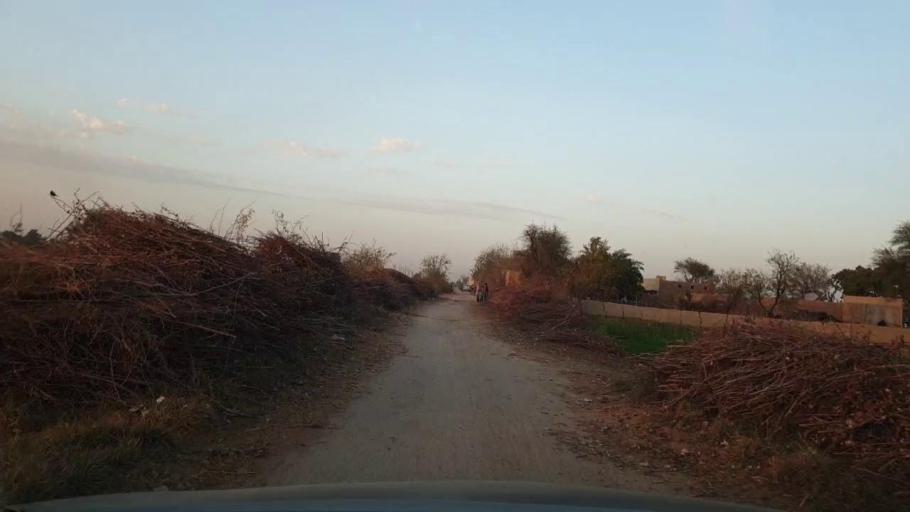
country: PK
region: Sindh
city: Matiari
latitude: 25.6002
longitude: 68.4796
